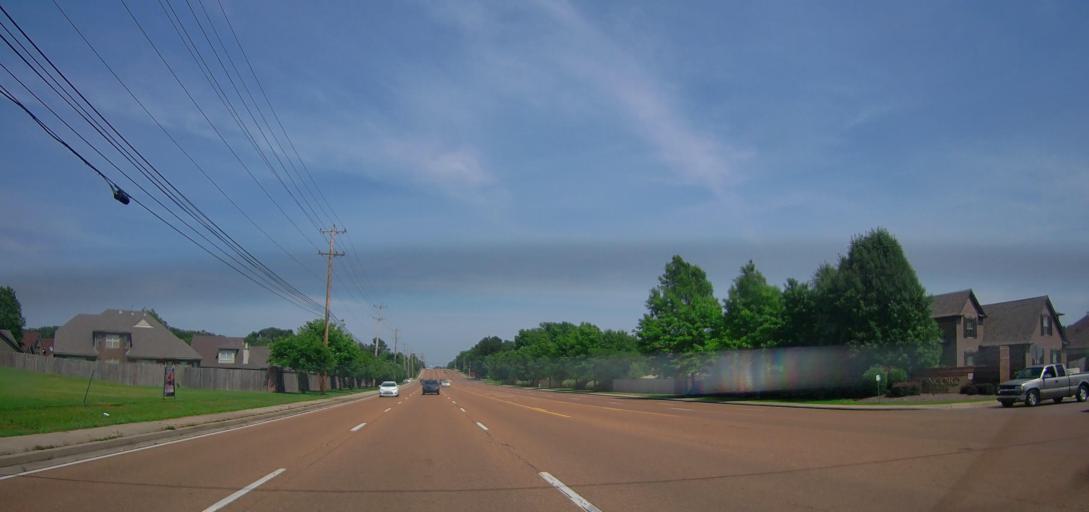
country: US
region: Mississippi
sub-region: De Soto County
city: Olive Branch
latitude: 35.0205
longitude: -89.8117
